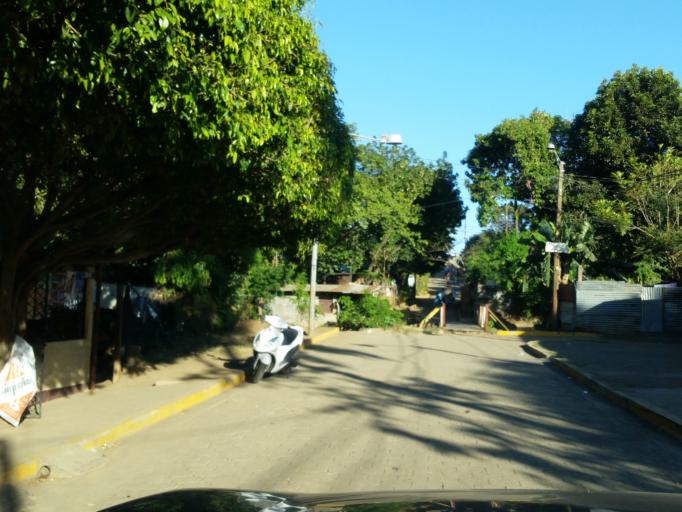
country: NI
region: Managua
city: Managua
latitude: 12.1127
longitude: -86.2887
